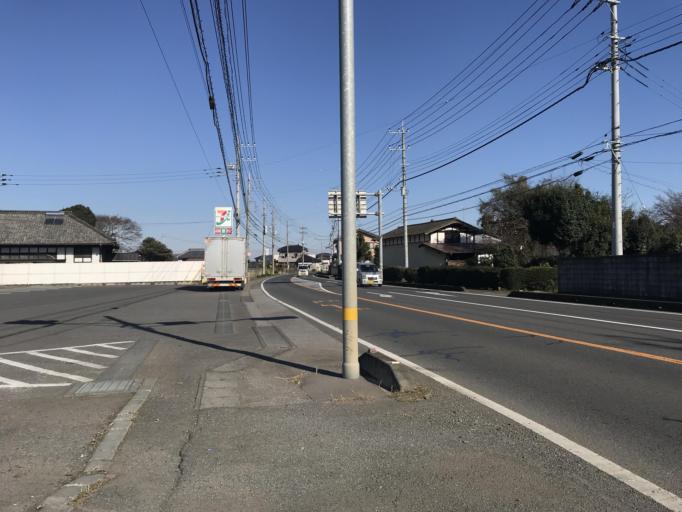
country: JP
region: Ibaraki
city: Yuki
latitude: 36.2741
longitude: 139.8489
